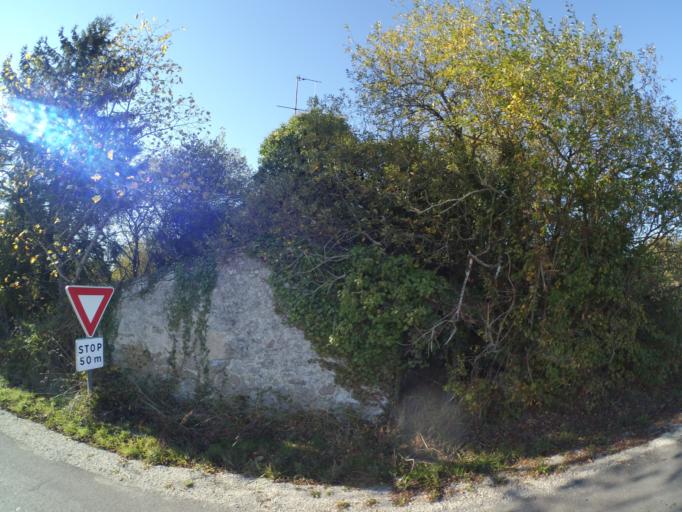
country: FR
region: Pays de la Loire
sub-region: Departement de la Loire-Atlantique
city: Saint-Lumine-de-Clisson
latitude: 47.0812
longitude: -1.3312
